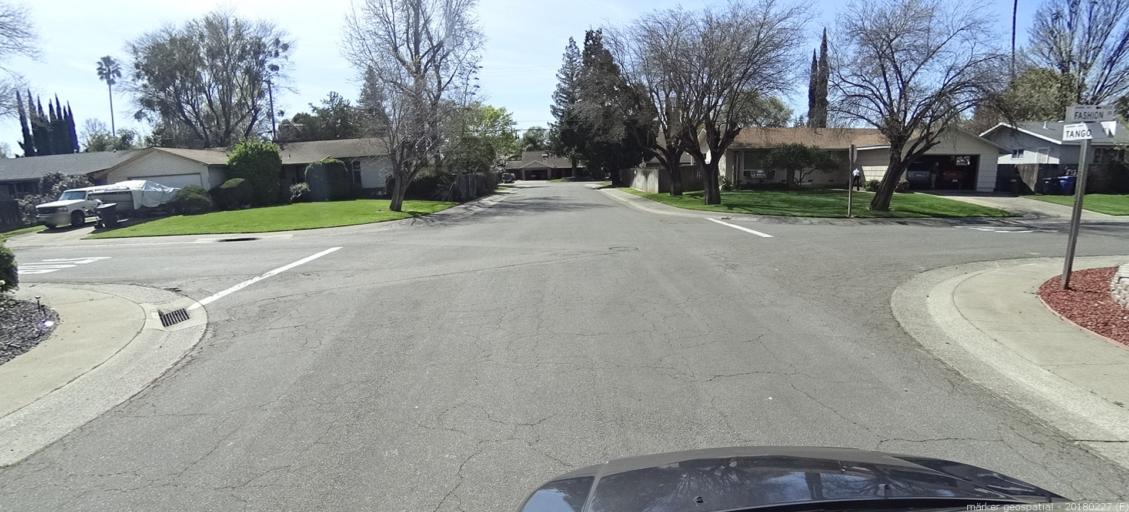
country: US
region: California
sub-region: Sacramento County
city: Rosemont
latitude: 38.5519
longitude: -121.3680
